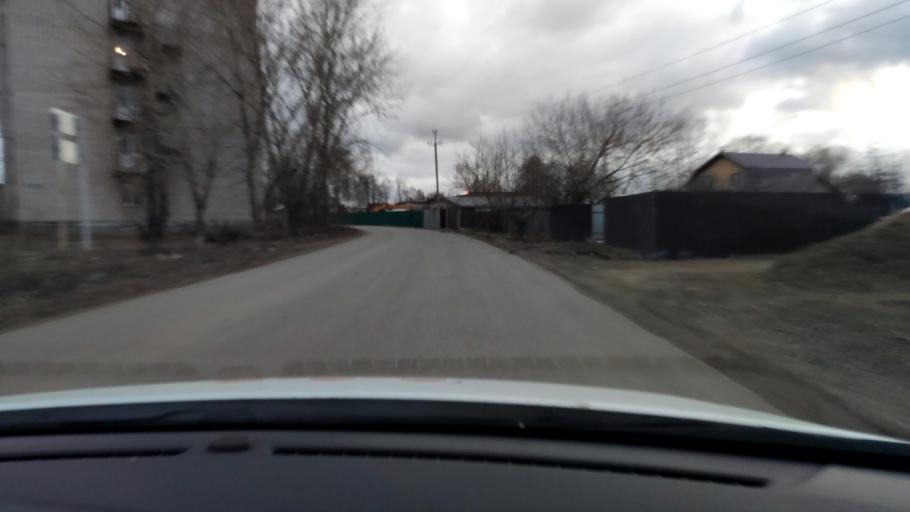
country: RU
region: Tatarstan
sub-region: Gorod Kazan'
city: Kazan
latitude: 55.7198
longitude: 49.0926
